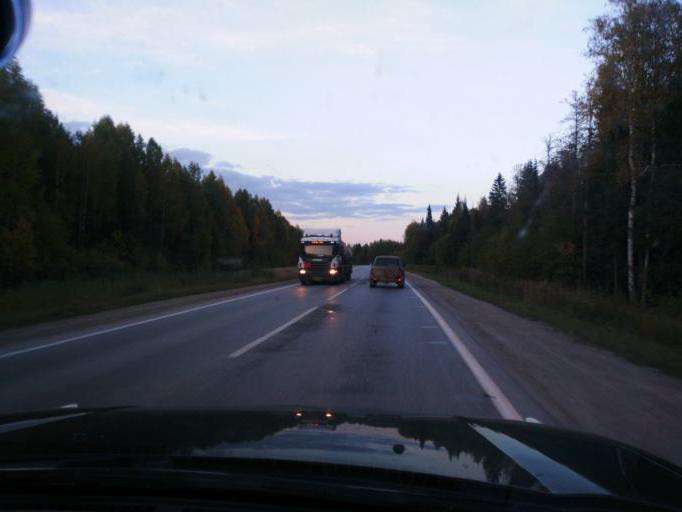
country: RU
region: Perm
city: Polazna
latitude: 58.3001
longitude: 56.5664
